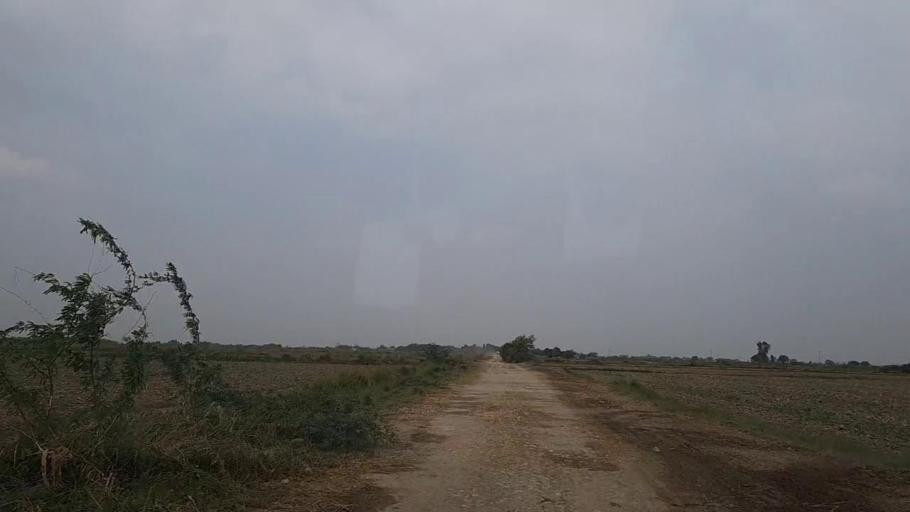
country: PK
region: Sindh
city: Mirpur Sakro
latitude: 24.5978
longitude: 67.6973
